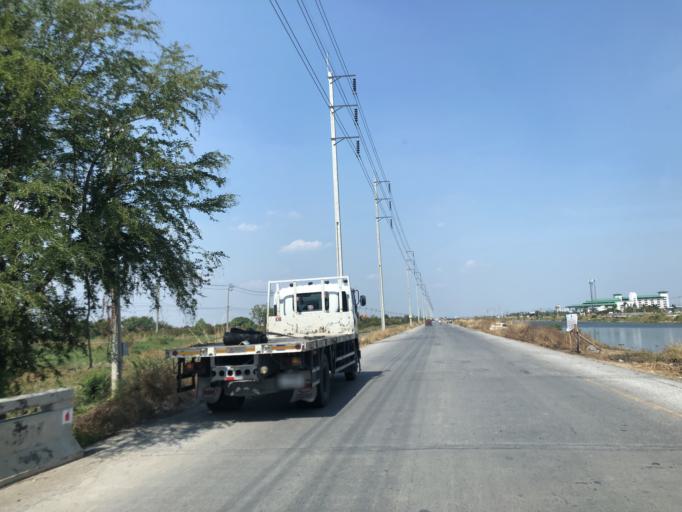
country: TH
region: Samut Prakan
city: Bang Bo District
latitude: 13.5185
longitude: 100.7465
